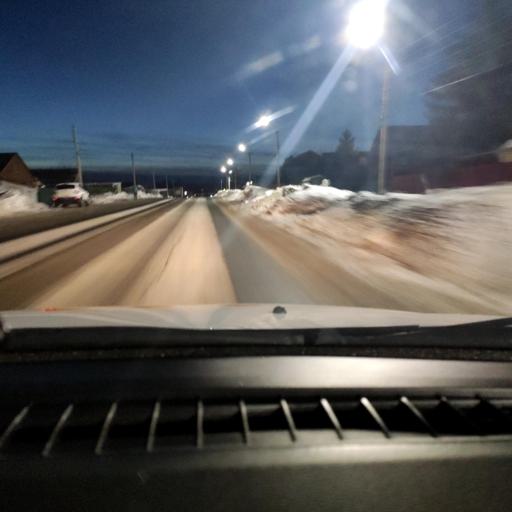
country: RU
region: Samara
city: Kinel'
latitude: 53.2690
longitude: 50.5839
